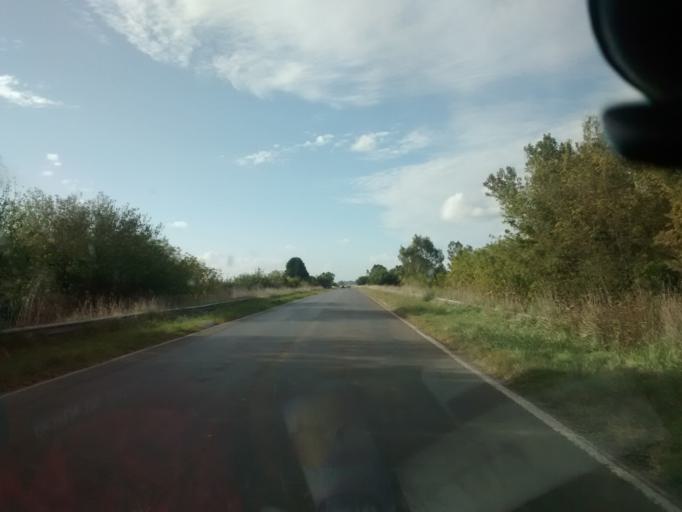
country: AR
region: Buenos Aires
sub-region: Partido de Ayacucho
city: Ayacucho
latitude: -36.7094
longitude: -58.5741
